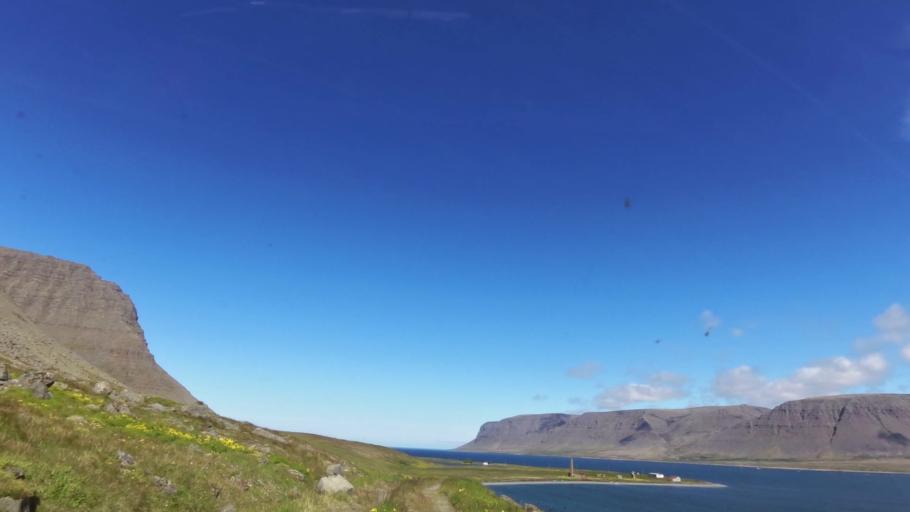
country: IS
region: West
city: Olafsvik
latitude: 65.6351
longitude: -23.9262
